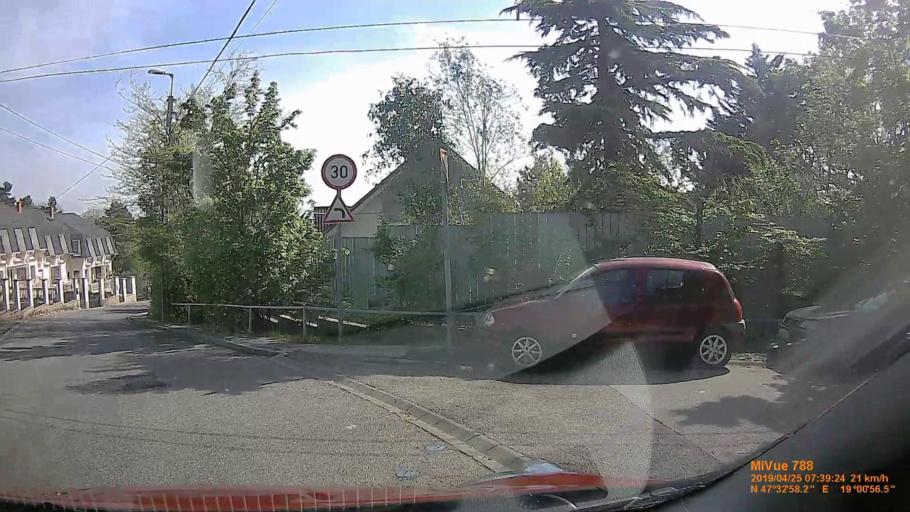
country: HU
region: Budapest
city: Budapest III. keruelet
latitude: 47.5495
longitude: 19.0161
